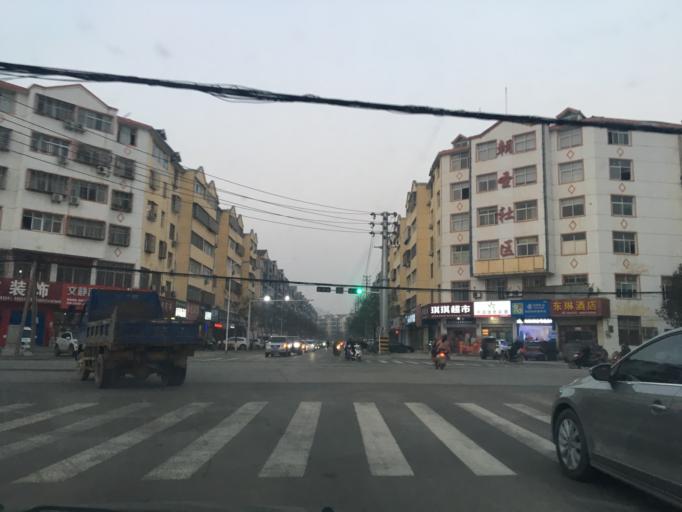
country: CN
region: Hubei
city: Gulou
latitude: 31.1697
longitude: 115.0307
